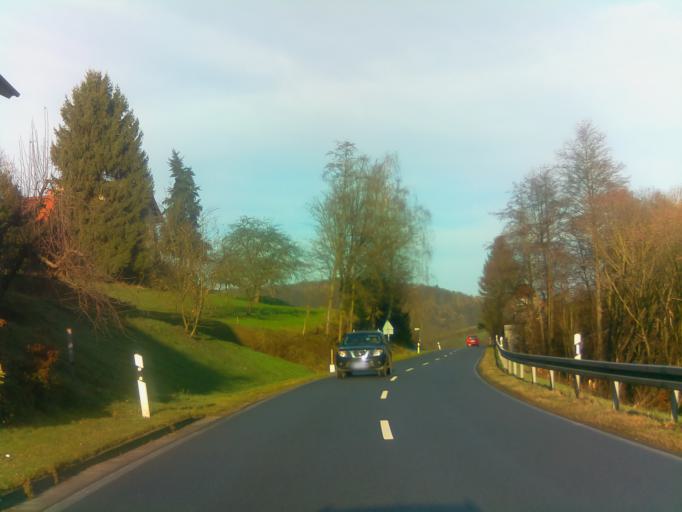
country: DE
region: Hesse
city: Reichelsheim
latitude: 49.6883
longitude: 8.8711
